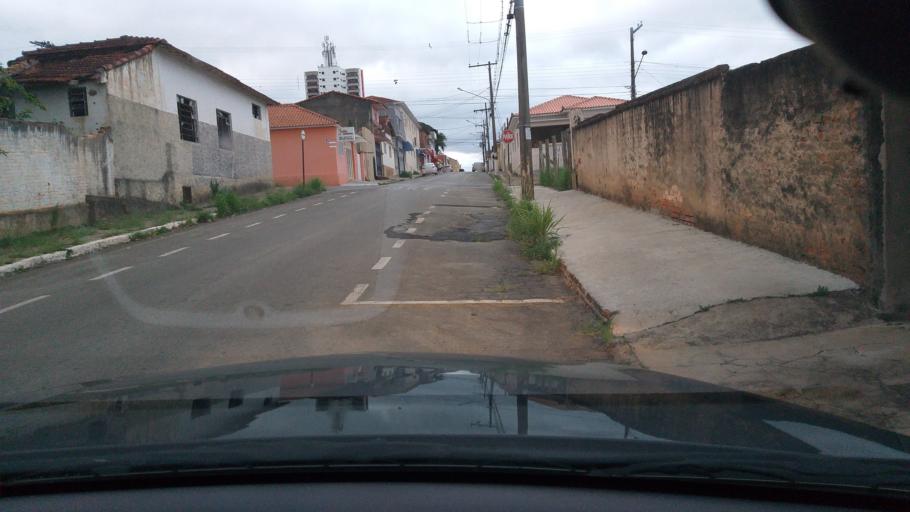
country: BR
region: Sao Paulo
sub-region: Itapeva
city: Itapeva
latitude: -23.9870
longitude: -48.8739
